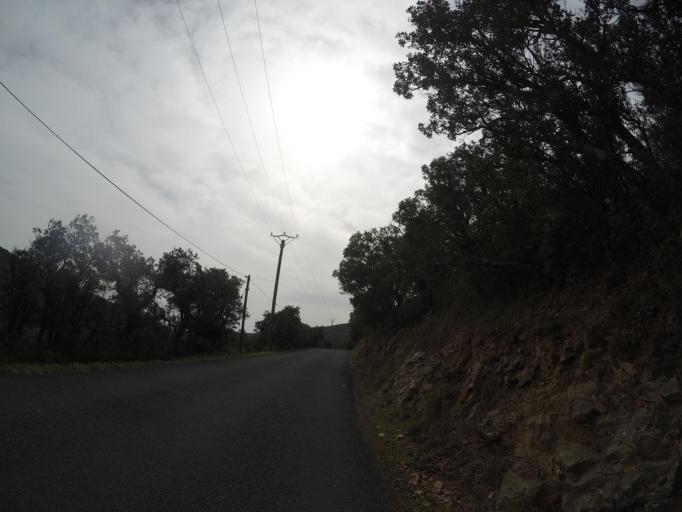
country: FR
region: Languedoc-Roussillon
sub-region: Departement des Pyrenees-Orientales
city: Corneilla-la-Riviere
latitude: 42.7337
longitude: 2.7332
